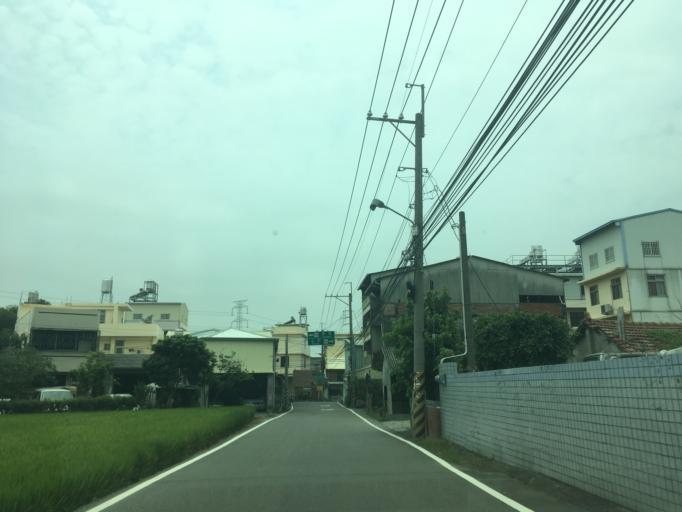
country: TW
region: Taiwan
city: Zhongxing New Village
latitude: 24.0265
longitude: 120.6913
